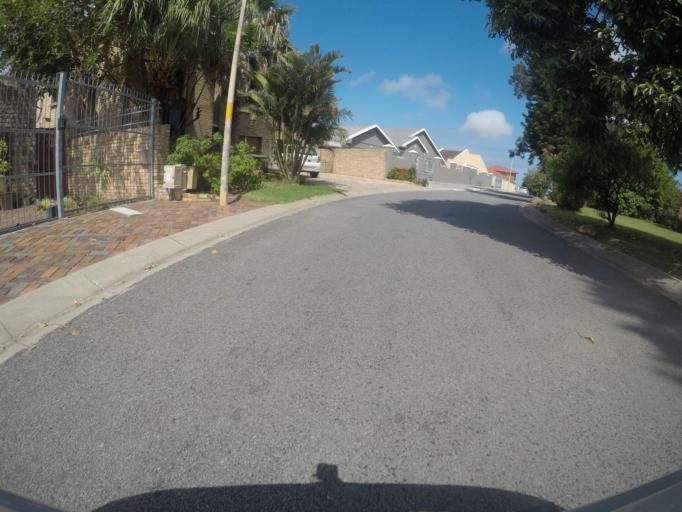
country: ZA
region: Eastern Cape
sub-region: Buffalo City Metropolitan Municipality
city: East London
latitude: -32.9975
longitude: 27.8871
